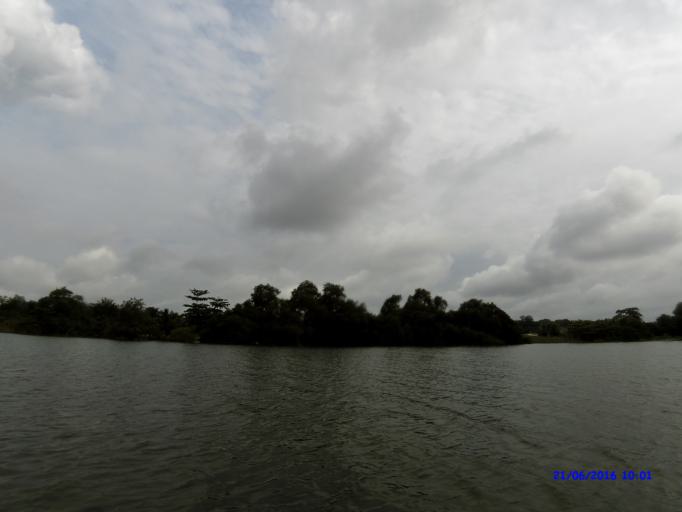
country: BJ
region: Mono
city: Come
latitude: 6.4521
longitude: 1.9246
